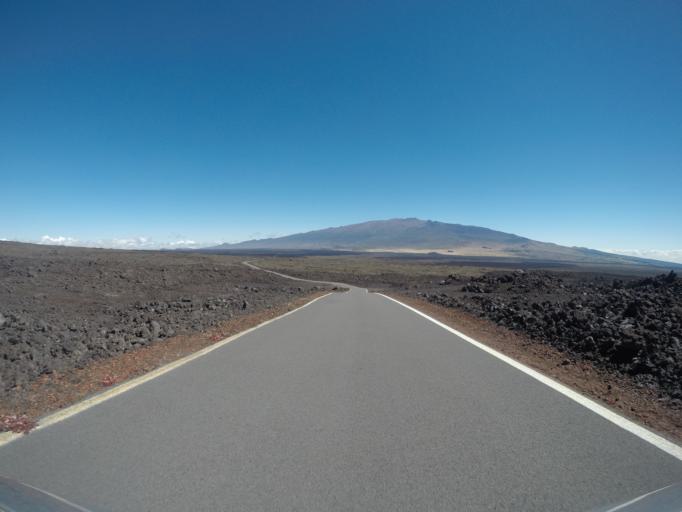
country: US
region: Hawaii
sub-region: Hawaii County
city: Volcano
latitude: 19.6190
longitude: -155.4725
